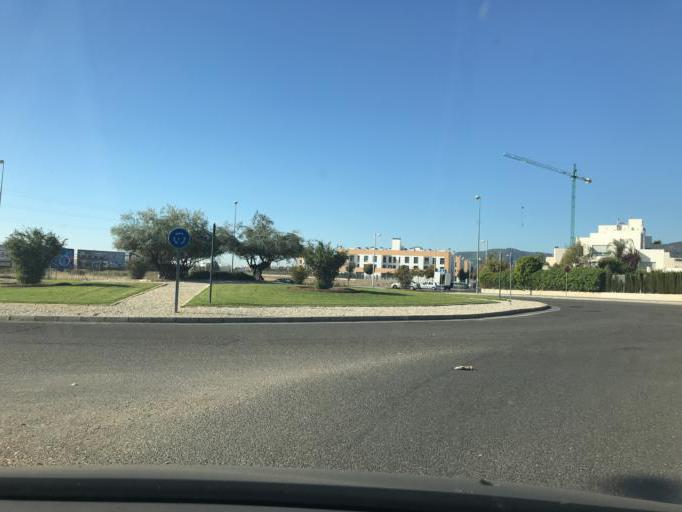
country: ES
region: Andalusia
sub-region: Province of Cordoba
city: Cordoba
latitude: 37.9000
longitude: -4.7988
